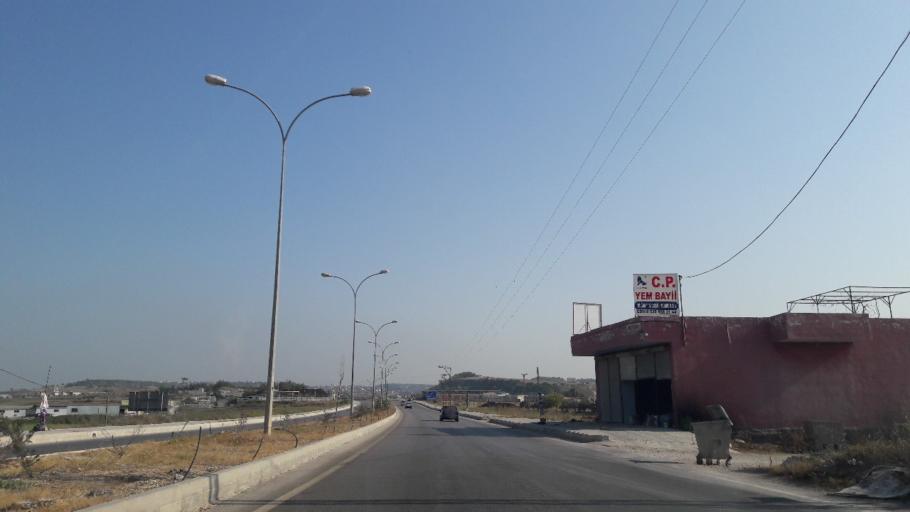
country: TR
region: Adana
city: Yuregir
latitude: 37.0480
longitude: 35.4373
